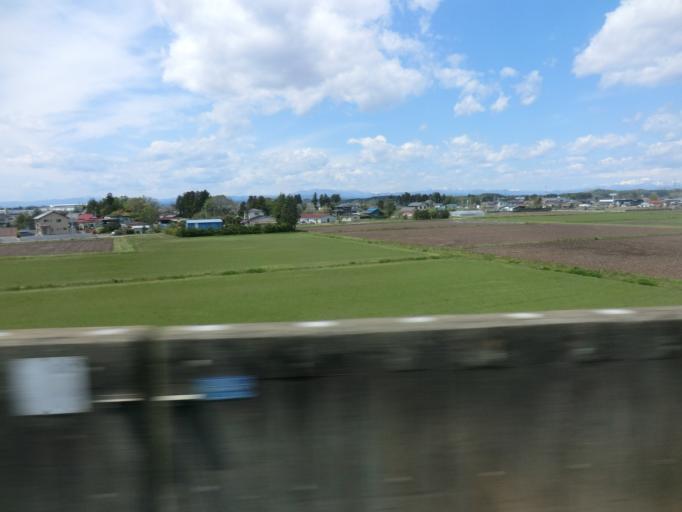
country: JP
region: Miyagi
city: Furukawa
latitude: 38.6041
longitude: 140.9850
